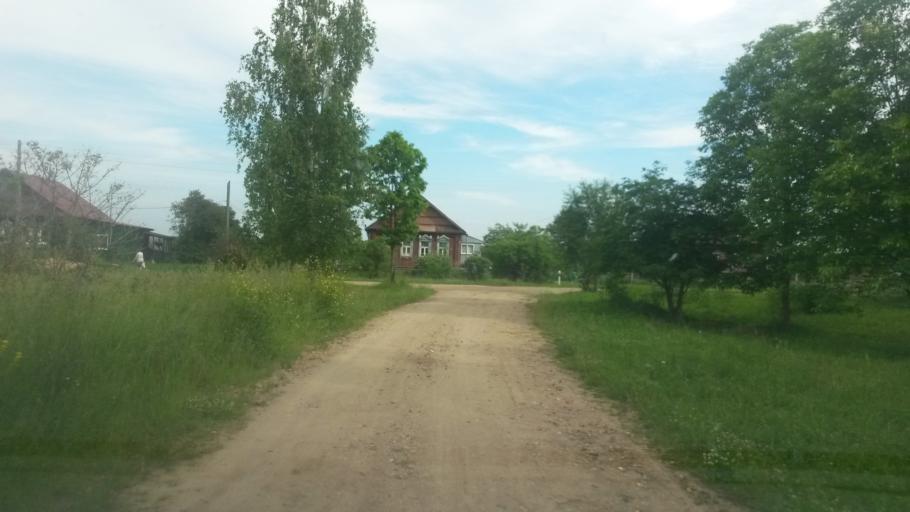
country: RU
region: Jaroslavl
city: Gavrilov-Yam
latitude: 57.3074
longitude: 39.9483
